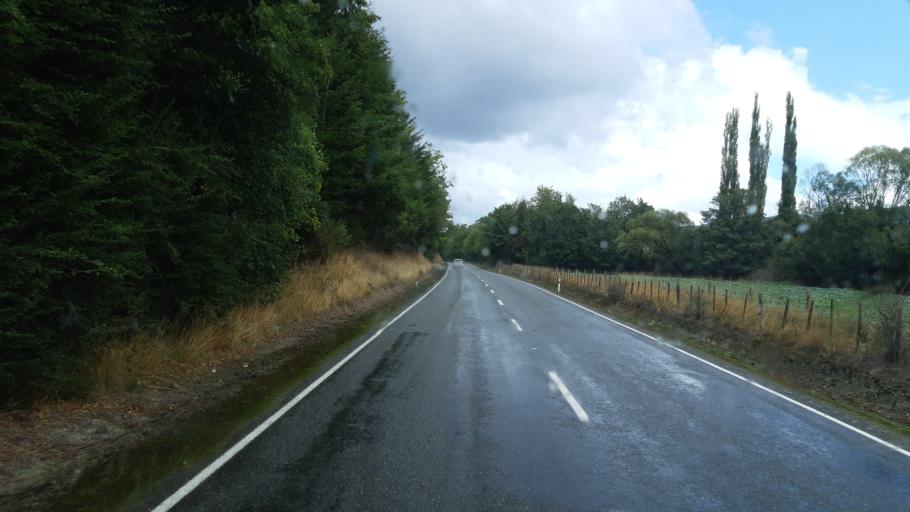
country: NZ
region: Tasman
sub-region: Tasman District
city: Wakefield
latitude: -41.4659
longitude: 172.8402
